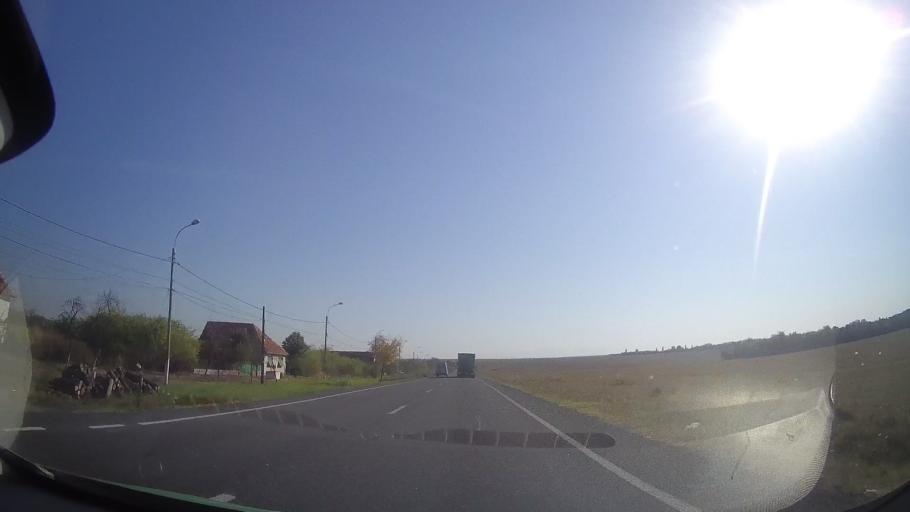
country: RO
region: Timis
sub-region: Comuna Topolovatu Mare
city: Topolovatu Mare
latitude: 45.7779
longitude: 21.6814
